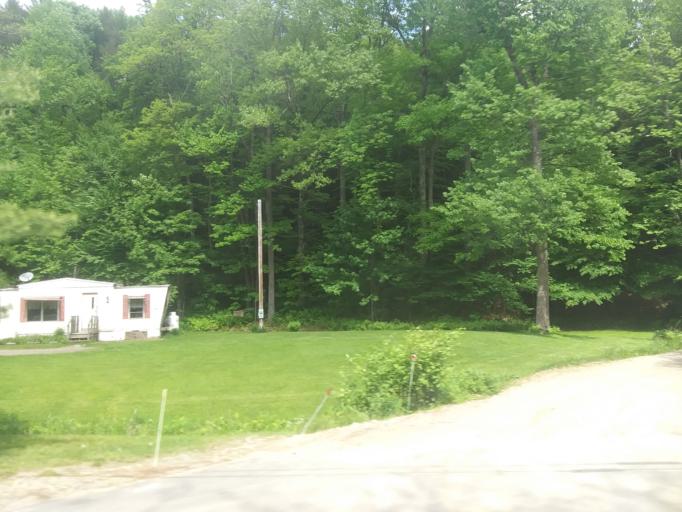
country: US
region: Massachusetts
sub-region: Franklin County
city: Buckland
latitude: 42.5682
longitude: -72.8095
